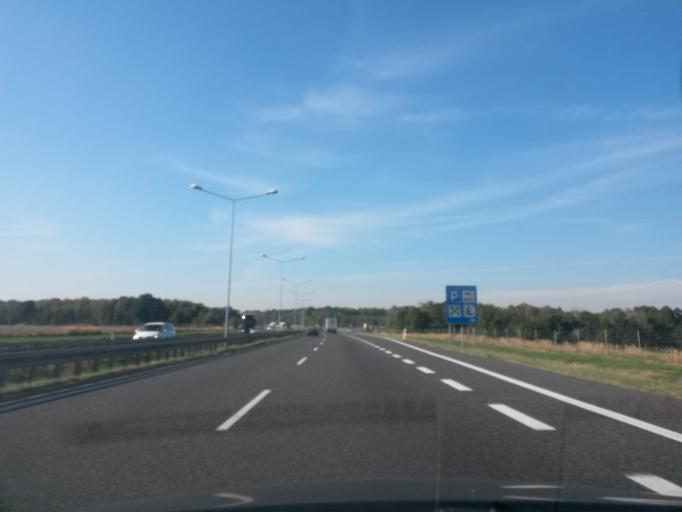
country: PL
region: Opole Voivodeship
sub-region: Powiat strzelecki
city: Ujazd
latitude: 50.4213
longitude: 18.3973
